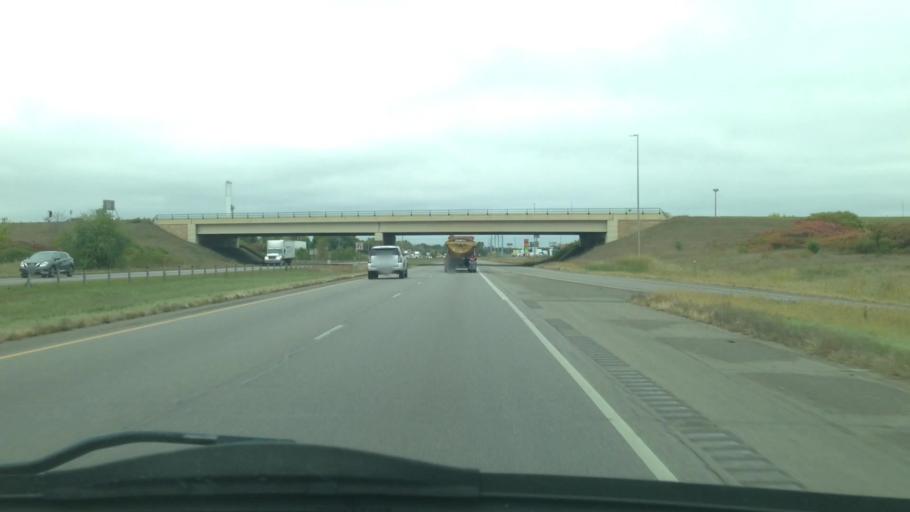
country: US
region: Minnesota
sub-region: Dakota County
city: Inver Grove Heights
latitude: 44.7768
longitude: -93.0347
